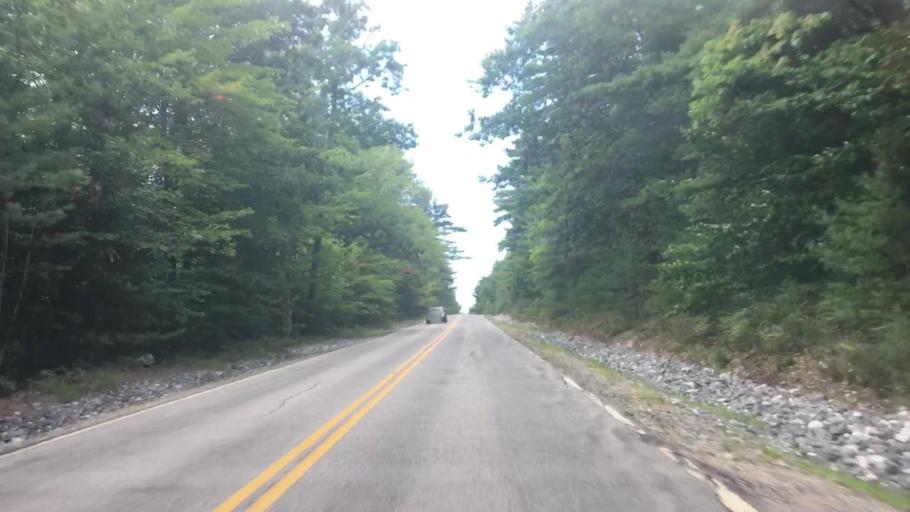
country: US
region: Maine
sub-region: Oxford County
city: Oxford
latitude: 44.0726
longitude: -70.5451
